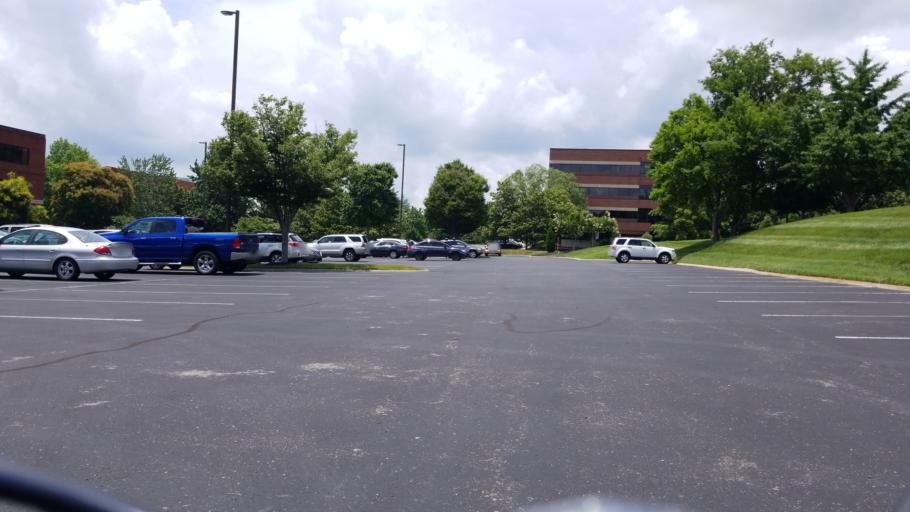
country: US
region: Tennessee
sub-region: Williamson County
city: Brentwood
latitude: 36.0376
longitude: -86.8094
